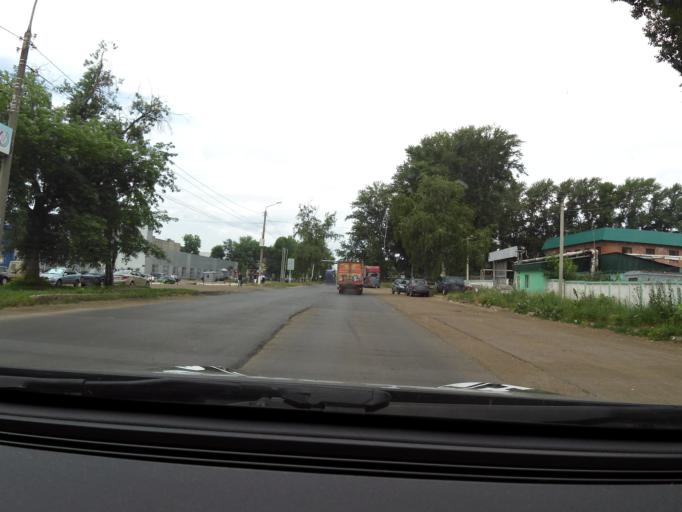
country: RU
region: Bashkortostan
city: Ufa
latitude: 54.8028
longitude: 56.1014
